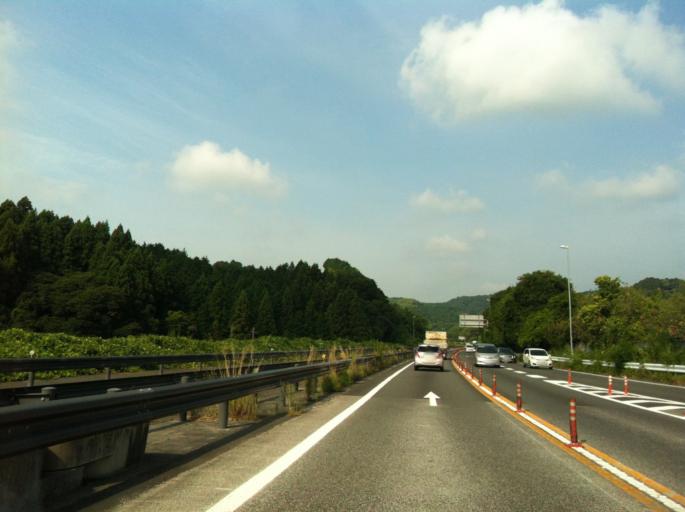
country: JP
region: Shizuoka
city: Fujieda
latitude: 34.8694
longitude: 138.2229
